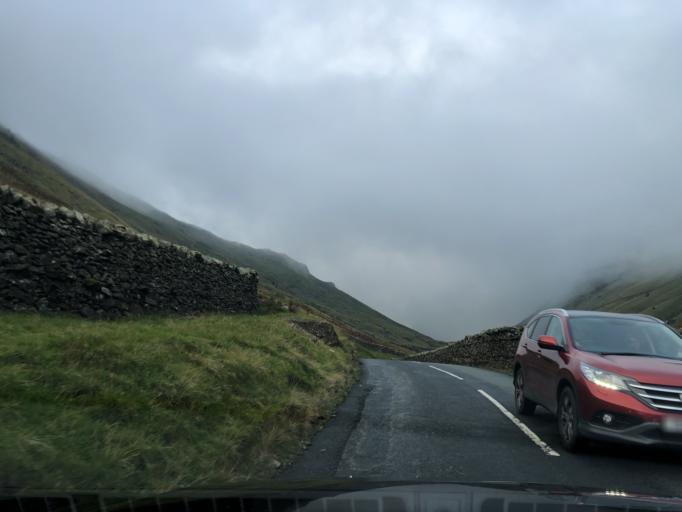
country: GB
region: England
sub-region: Cumbria
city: Ambleside
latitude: 54.4786
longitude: -2.9222
